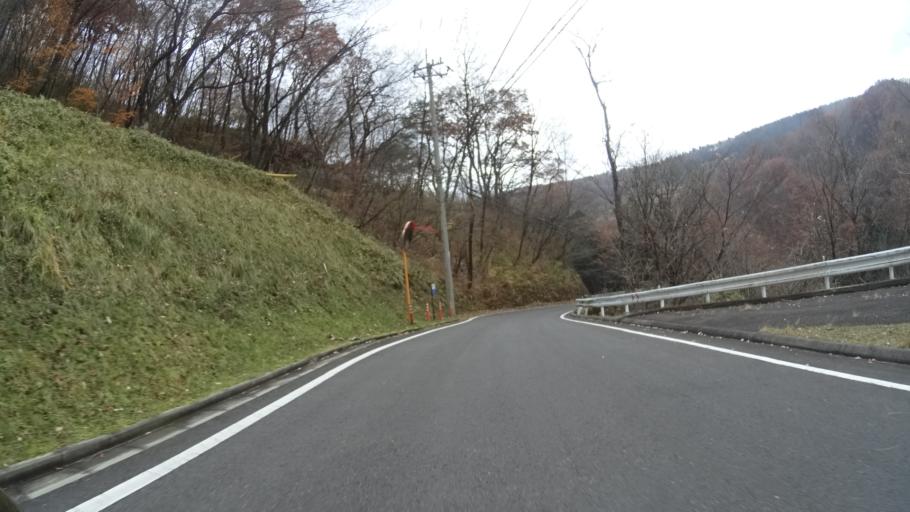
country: JP
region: Gunma
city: Omamacho-omama
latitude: 36.4947
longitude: 139.1846
